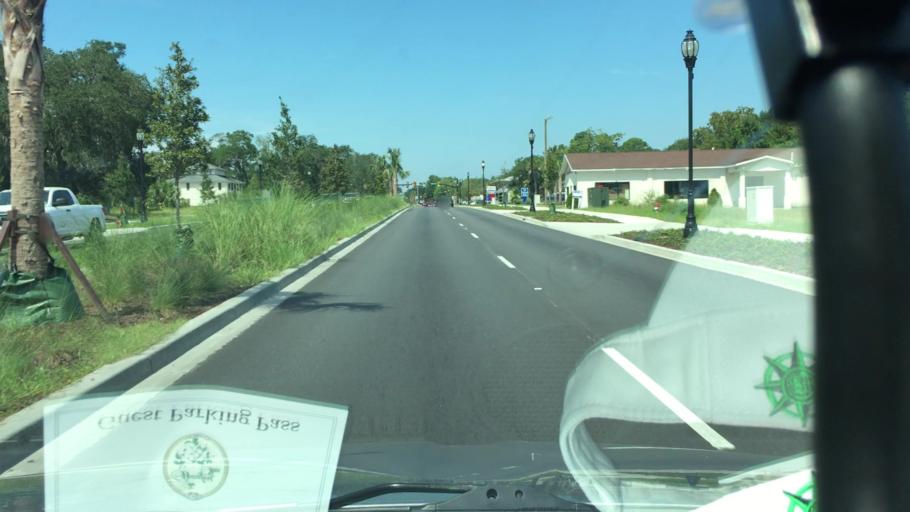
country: US
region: South Carolina
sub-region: Beaufort County
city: Burton
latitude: 32.4415
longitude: -80.6968
